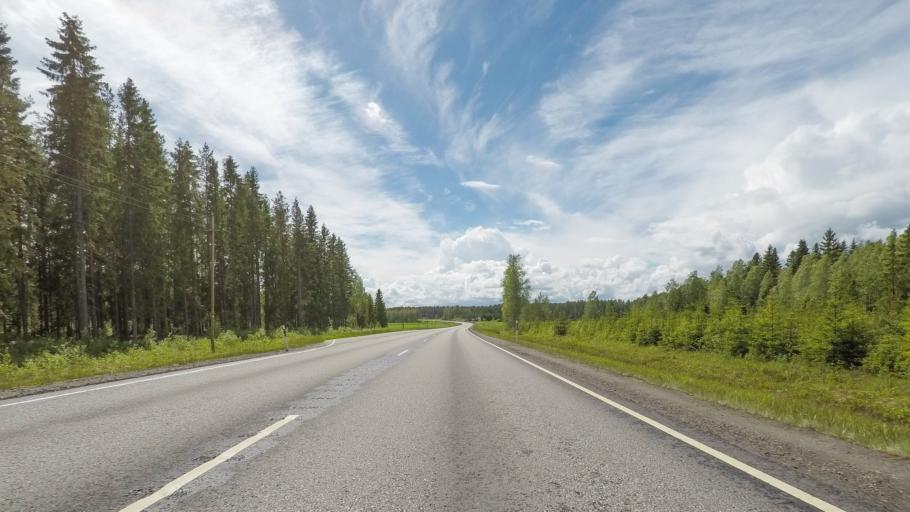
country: FI
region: Central Finland
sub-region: Jyvaeskylae
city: Hankasalmi
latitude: 62.3817
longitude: 26.5988
